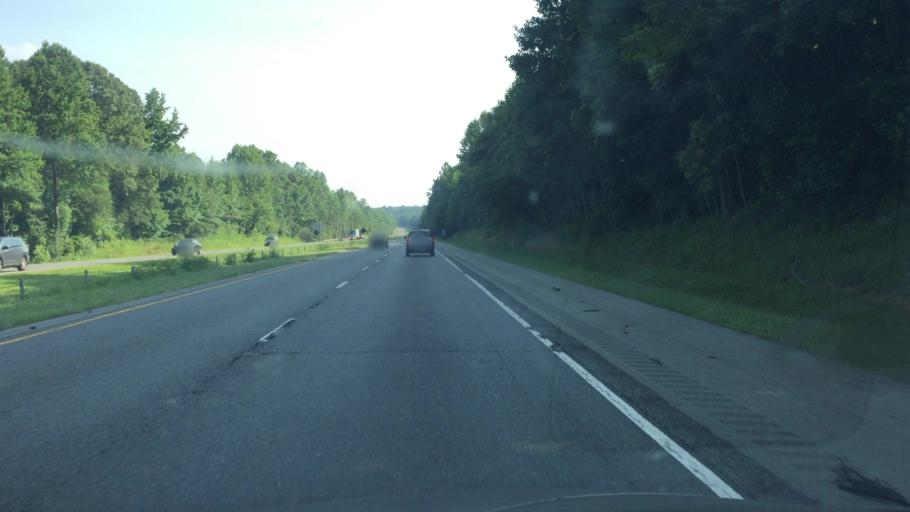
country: US
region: North Carolina
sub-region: Rockingham County
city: Reidsville
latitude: 36.3531
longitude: -79.6318
